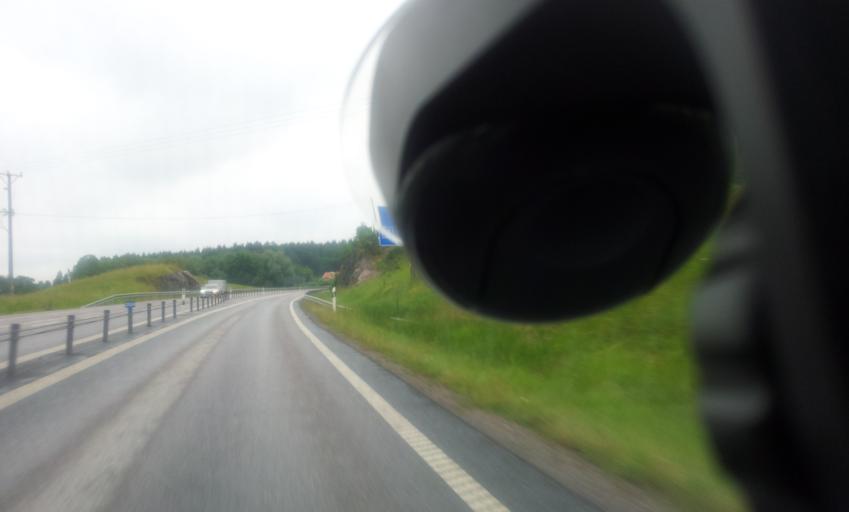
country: SE
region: Kalmar
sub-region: Vasterviks Kommun
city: Forserum
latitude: 57.9544
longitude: 16.4431
